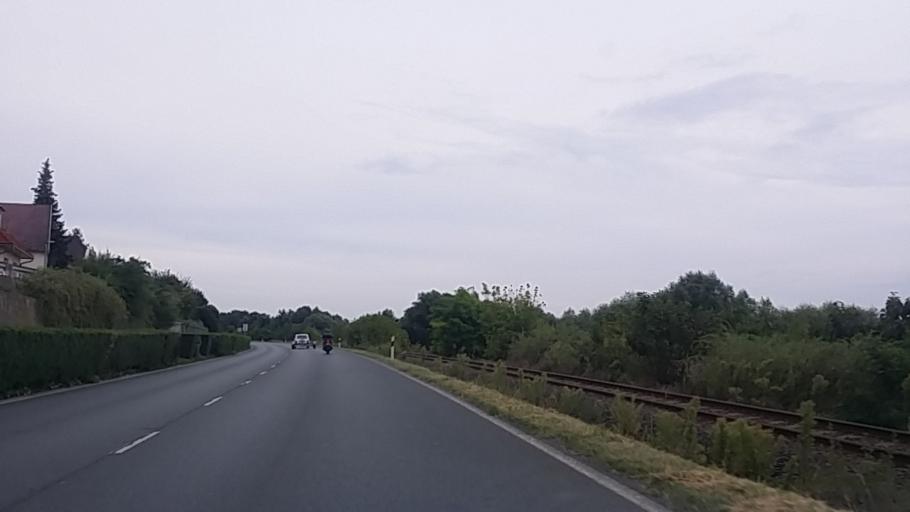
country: HU
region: Tolna
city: Paks
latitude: 46.6312
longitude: 18.8736
